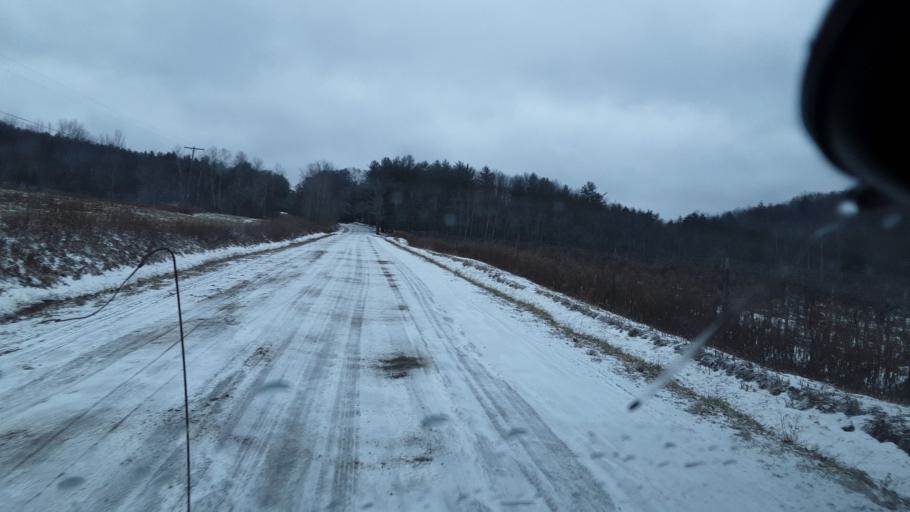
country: US
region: New York
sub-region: Allegany County
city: Friendship
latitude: 42.2893
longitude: -78.1624
